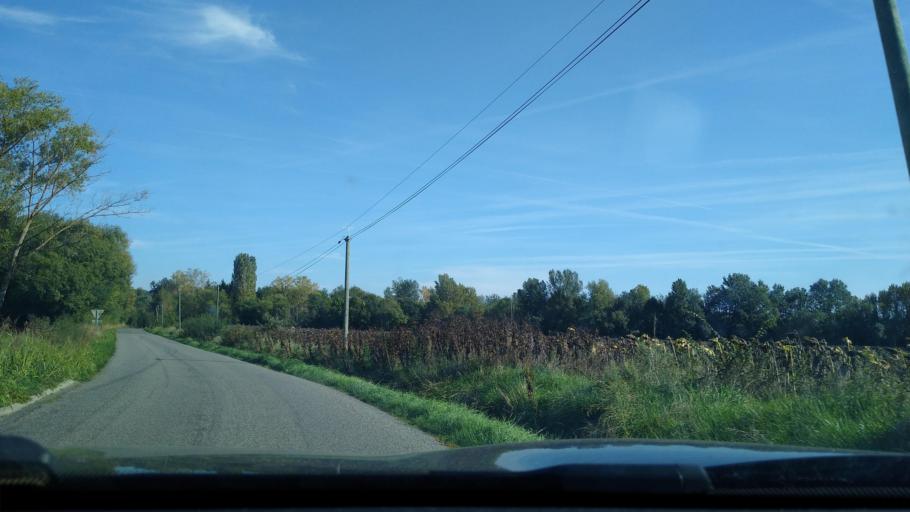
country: FR
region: Midi-Pyrenees
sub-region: Departement de la Haute-Garonne
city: Montaigut-sur-Save
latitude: 43.7287
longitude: 1.2387
